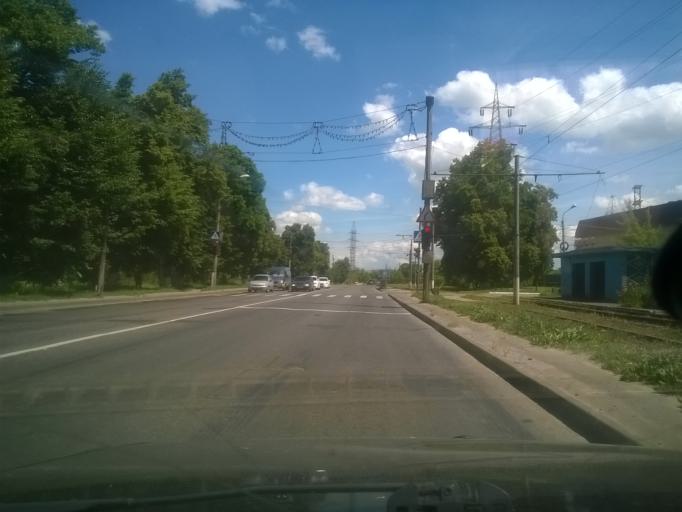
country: RU
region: Kursk
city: Voroshnevo
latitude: 51.6666
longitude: 36.1127
